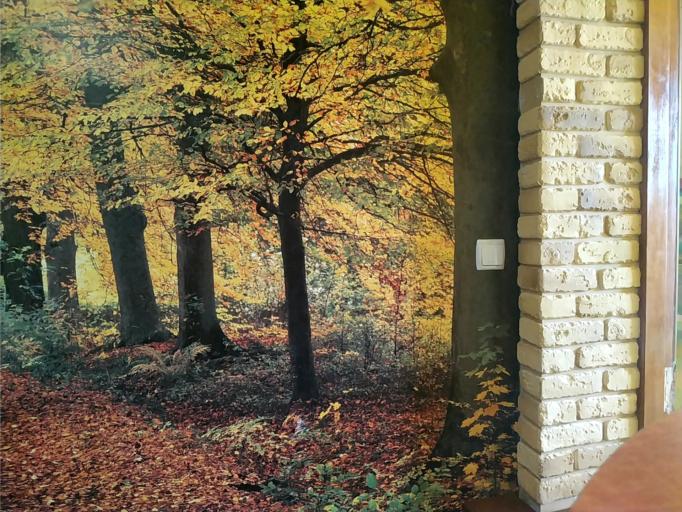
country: RU
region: Vologda
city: Nelazskoye
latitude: 59.4598
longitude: 37.6062
